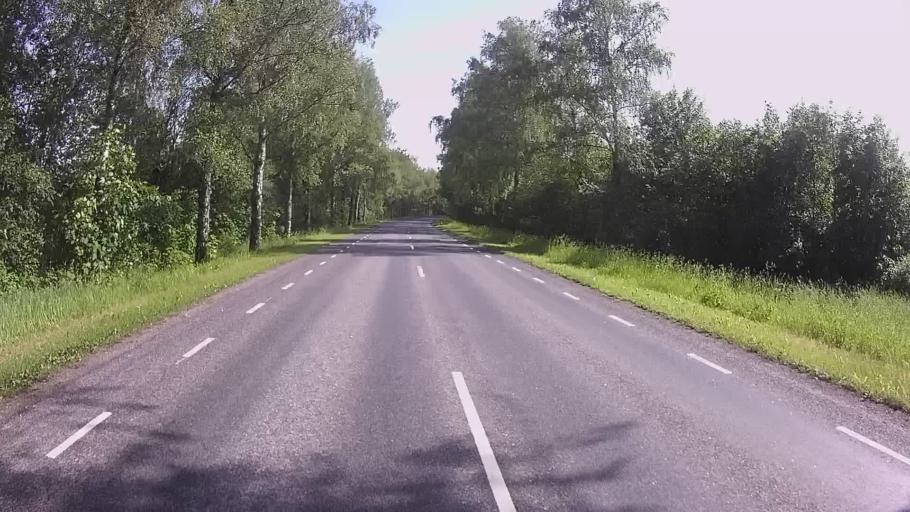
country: EE
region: Valgamaa
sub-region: Torva linn
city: Torva
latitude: 58.0722
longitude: 26.0359
